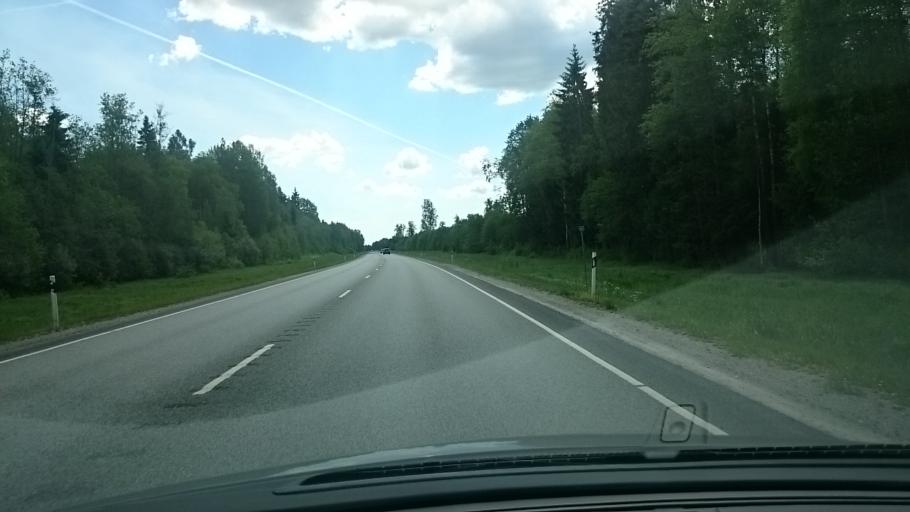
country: EE
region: Jaervamaa
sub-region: Paide linn
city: Paide
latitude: 59.0494
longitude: 25.4330
